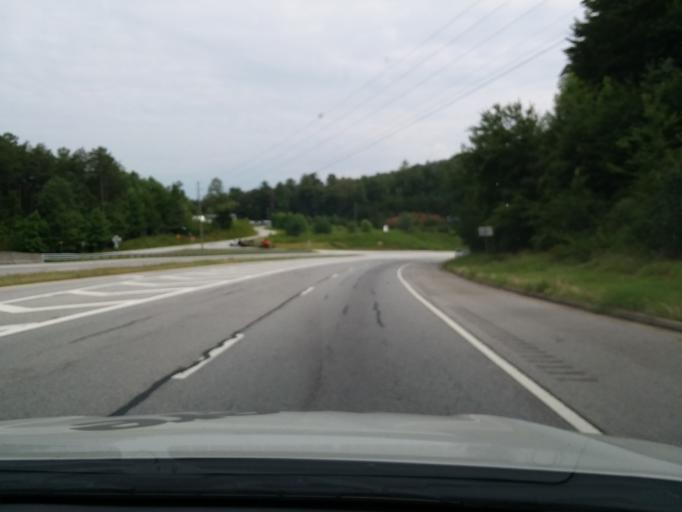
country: US
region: Georgia
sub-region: Rabun County
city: Clayton
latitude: 34.8290
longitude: -83.4260
